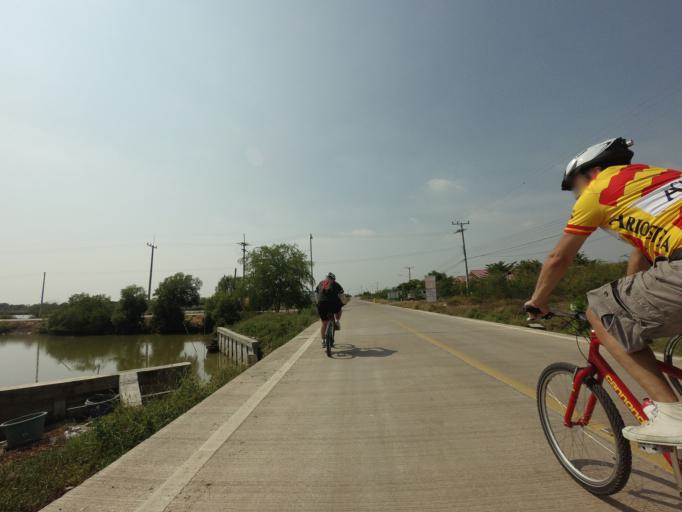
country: TH
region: Samut Sakhon
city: Samut Sakhon
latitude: 13.5131
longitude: 100.3897
